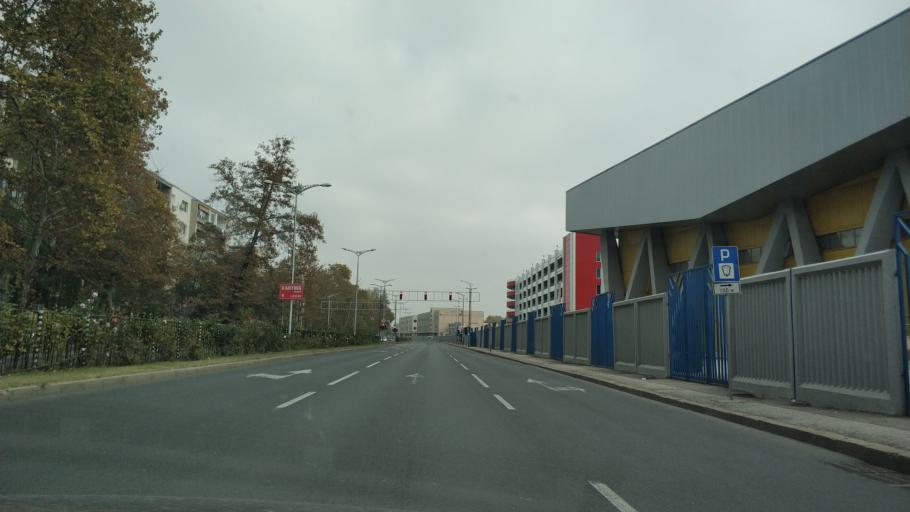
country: BG
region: Plovdiv
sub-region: Obshtina Plovdiv
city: Plovdiv
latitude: 42.1592
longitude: 24.7547
